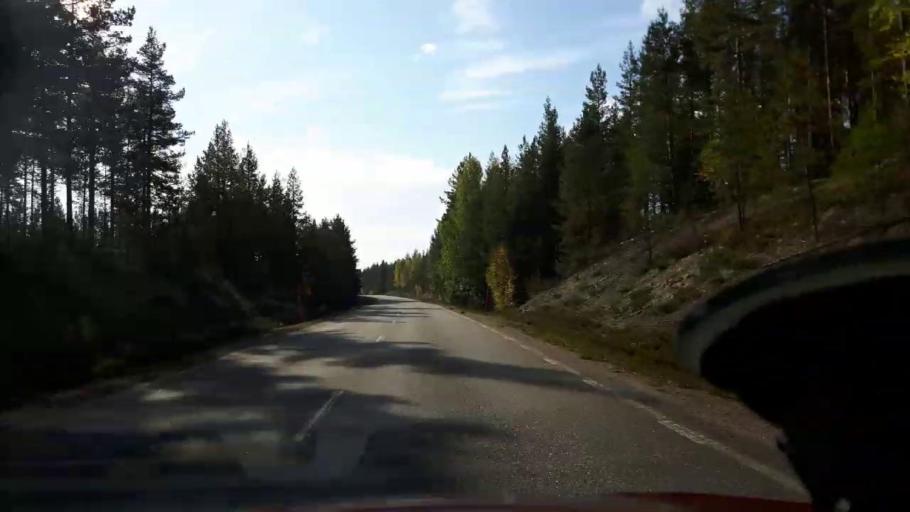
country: SE
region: Vaesternorrland
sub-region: Ange Kommun
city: Ange
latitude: 62.0721
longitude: 15.1027
